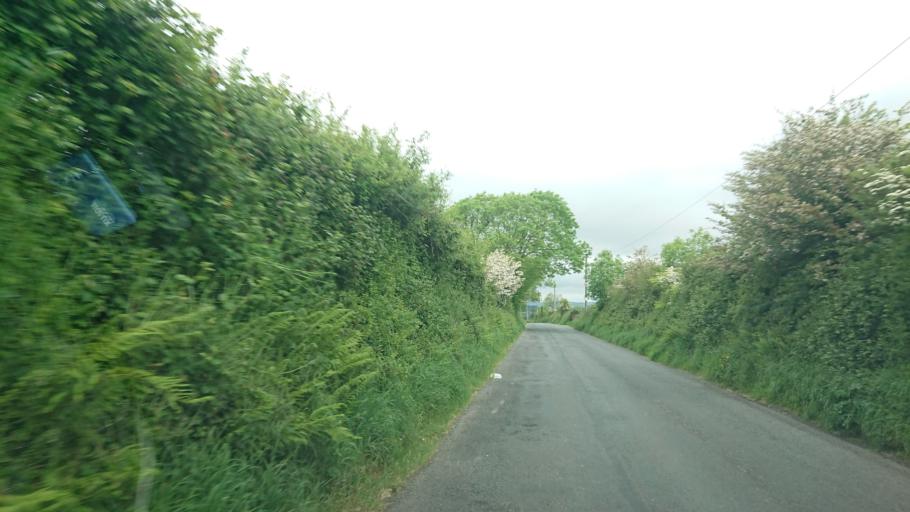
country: IE
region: Leinster
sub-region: Kilkenny
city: Mooncoin
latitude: 52.2379
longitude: -7.2017
